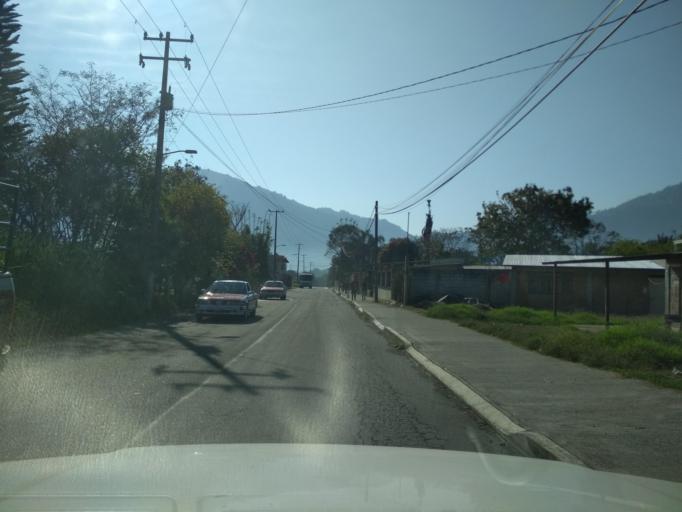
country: MX
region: Veracruz
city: Jalapilla
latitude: 18.8196
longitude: -97.0805
